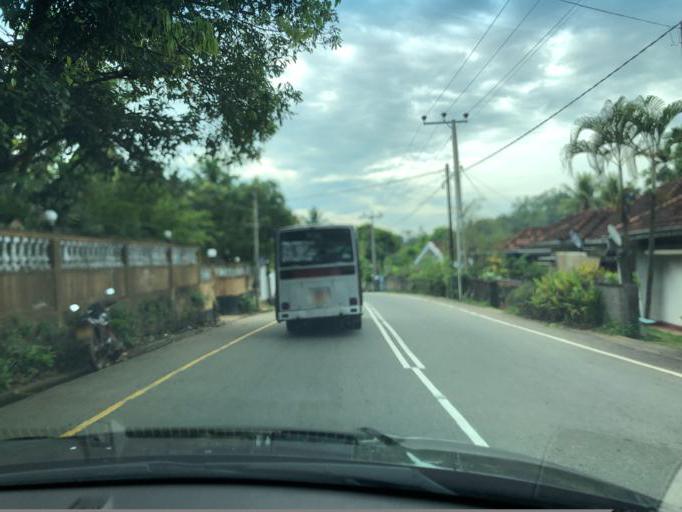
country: LK
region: Western
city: Kalutara
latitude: 6.5533
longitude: 80.0258
